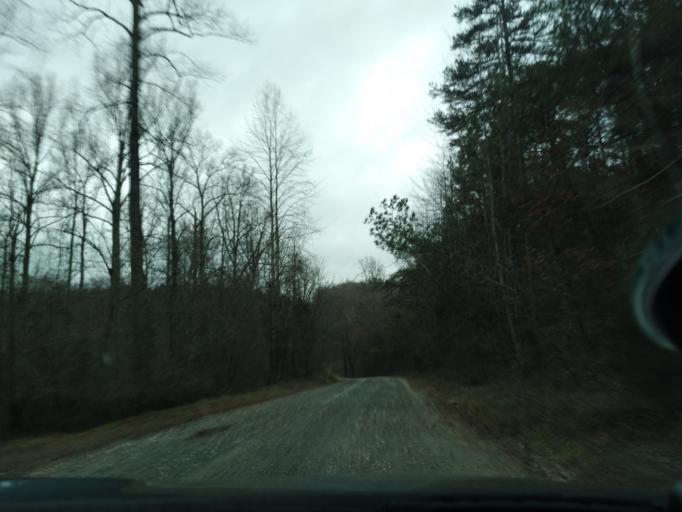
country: US
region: Virginia
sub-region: Buckingham County
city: Buckingham
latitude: 37.4247
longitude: -78.6584
